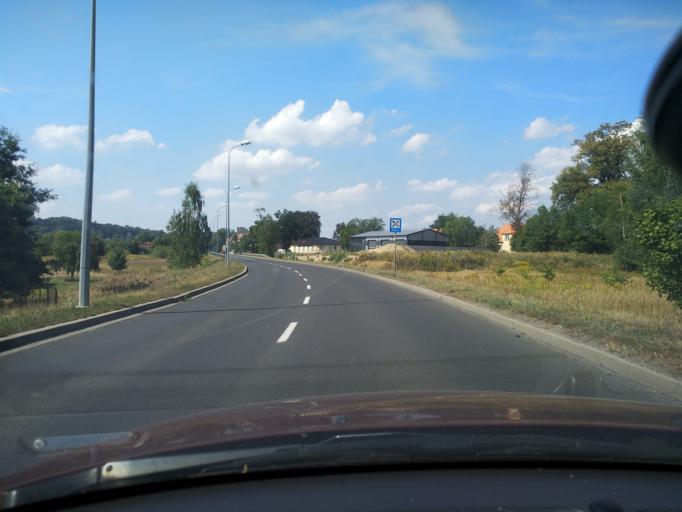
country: PL
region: Lower Silesian Voivodeship
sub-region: Powiat lubanski
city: Luban
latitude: 51.1077
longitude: 15.3044
